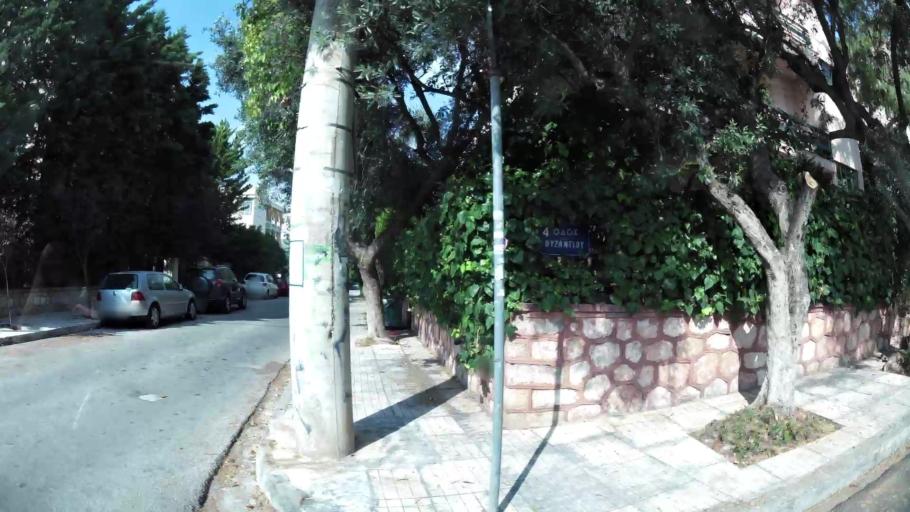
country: GR
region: Attica
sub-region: Nomarchia Athinas
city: Papagou
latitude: 37.9912
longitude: 23.7948
